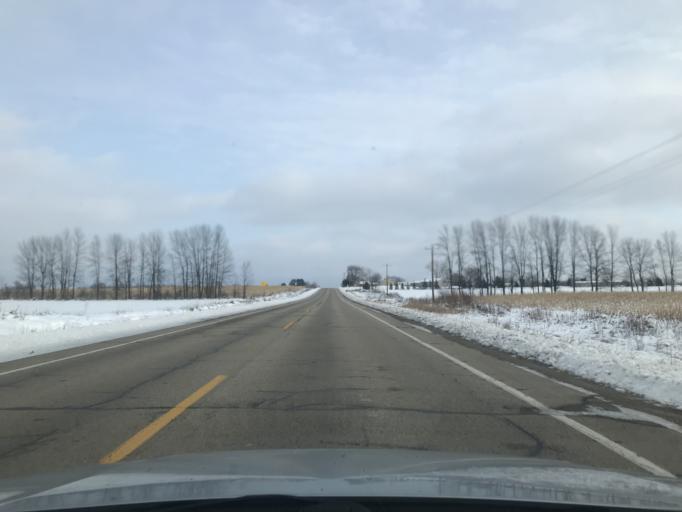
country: US
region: Wisconsin
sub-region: Oconto County
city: Oconto
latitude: 44.8930
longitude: -87.9754
